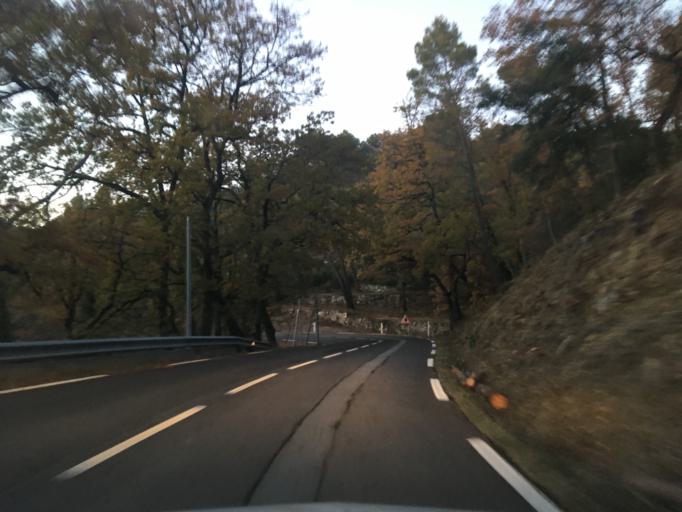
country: FR
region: Provence-Alpes-Cote d'Azur
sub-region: Departement du Var
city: Figanieres
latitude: 43.5362
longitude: 6.5040
